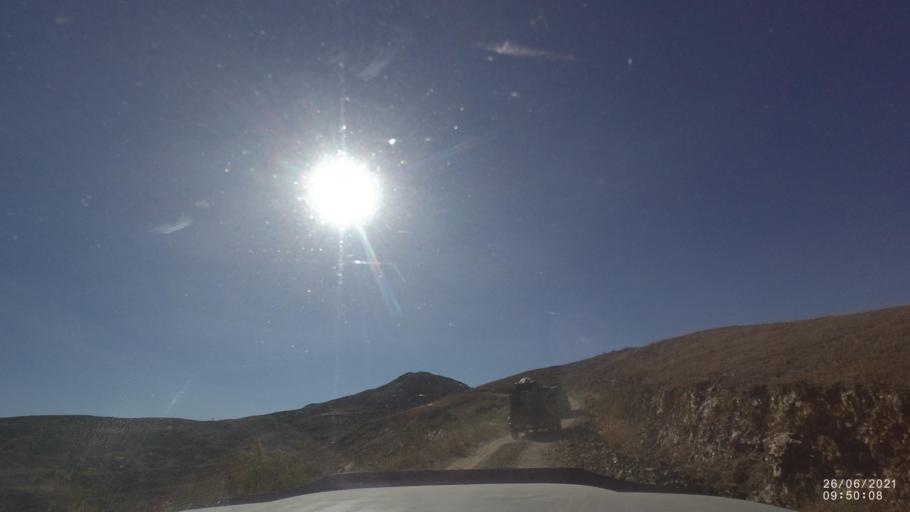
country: BO
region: Cochabamba
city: Mizque
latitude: -17.9496
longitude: -65.6262
